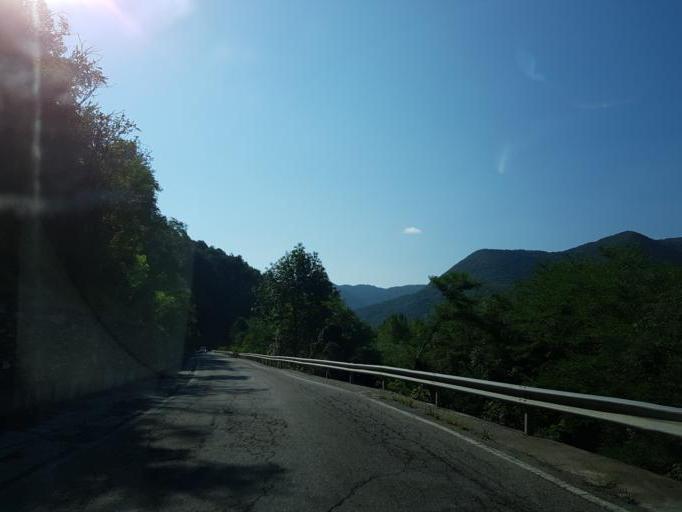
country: IT
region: Piedmont
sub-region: Provincia di Cuneo
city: Cartignano
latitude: 44.4744
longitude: 7.3042
